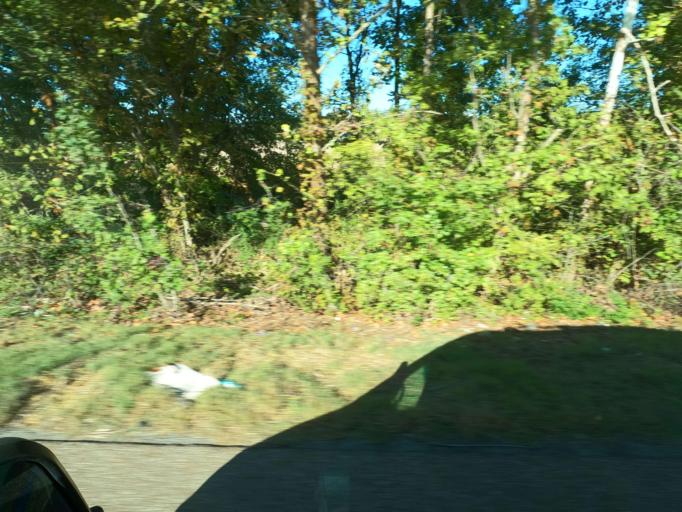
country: US
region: Tennessee
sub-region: Tipton County
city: Brighton
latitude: 35.5094
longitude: -89.7115
